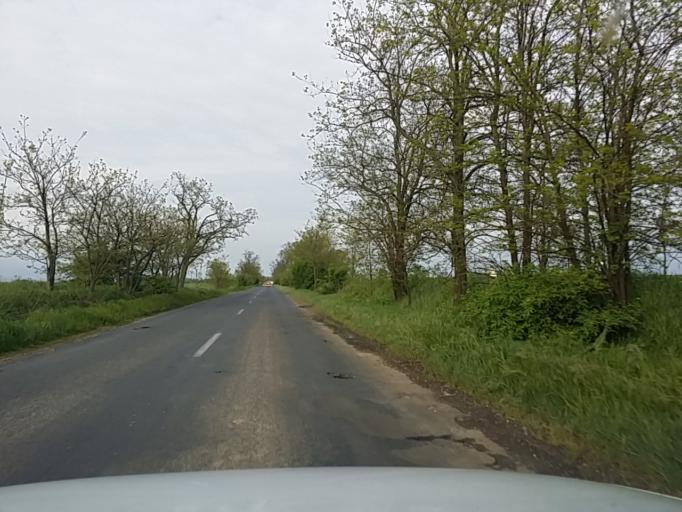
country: HU
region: Pest
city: Zsambok
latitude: 47.5397
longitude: 19.5897
